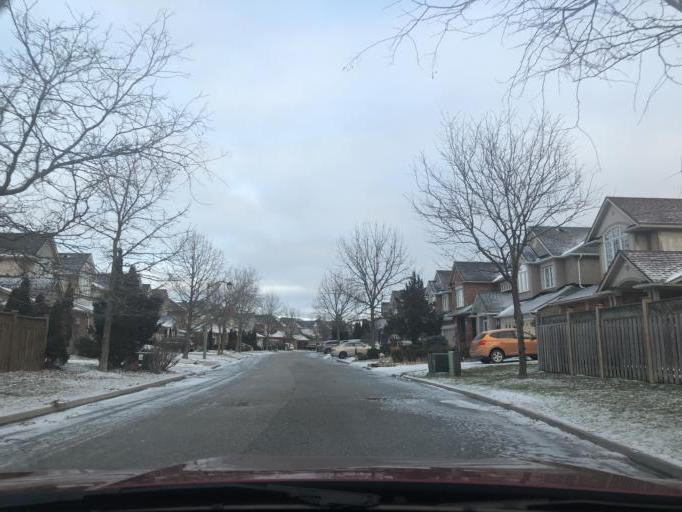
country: CA
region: Ontario
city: Markham
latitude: 43.8652
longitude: -79.2397
